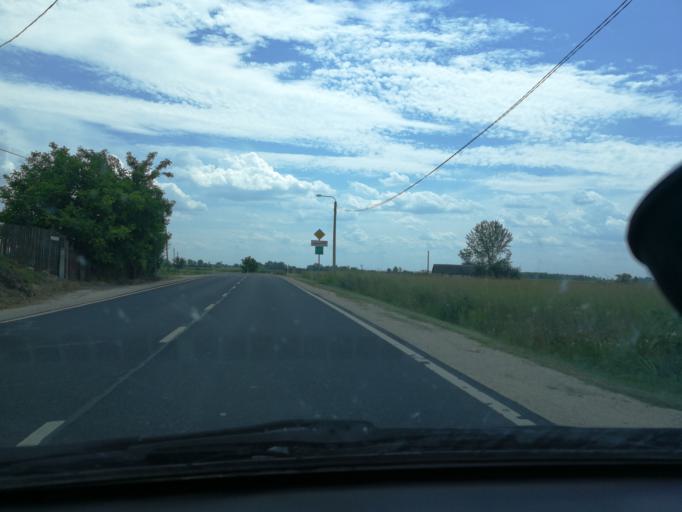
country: HU
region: Bacs-Kiskun
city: Kalocsa
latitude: 46.5748
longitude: 18.9750
